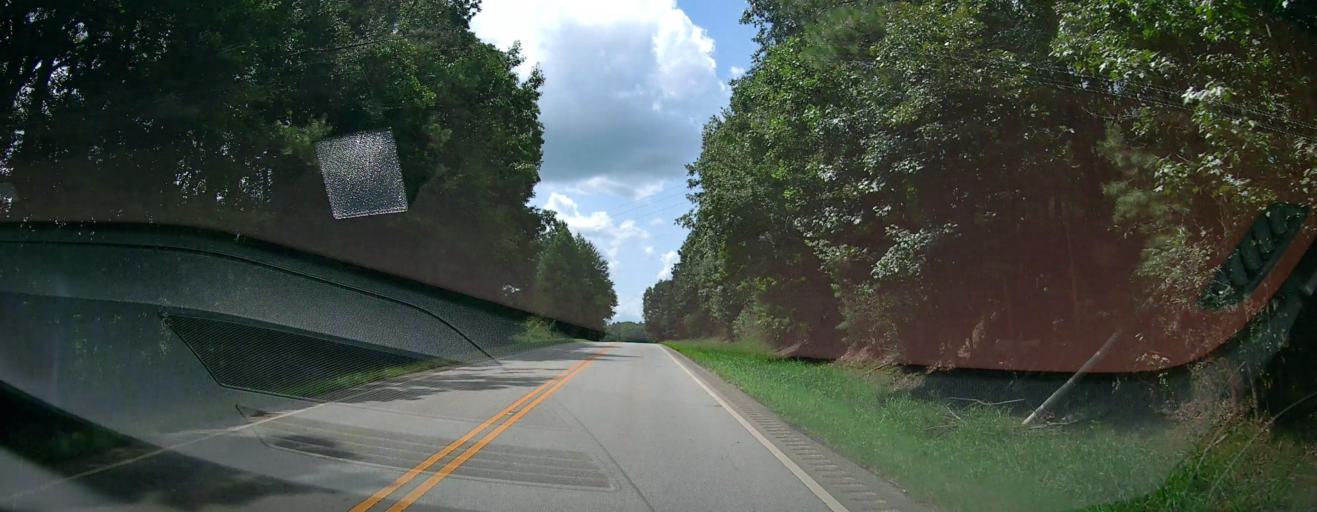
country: US
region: Georgia
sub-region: Carroll County
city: Bowdon
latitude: 33.5455
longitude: -85.3987
